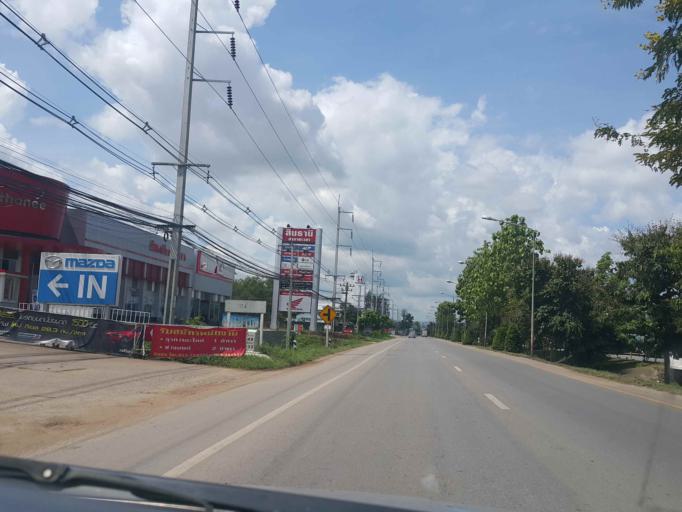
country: TH
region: Phayao
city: Phayao
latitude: 19.1510
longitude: 99.9127
